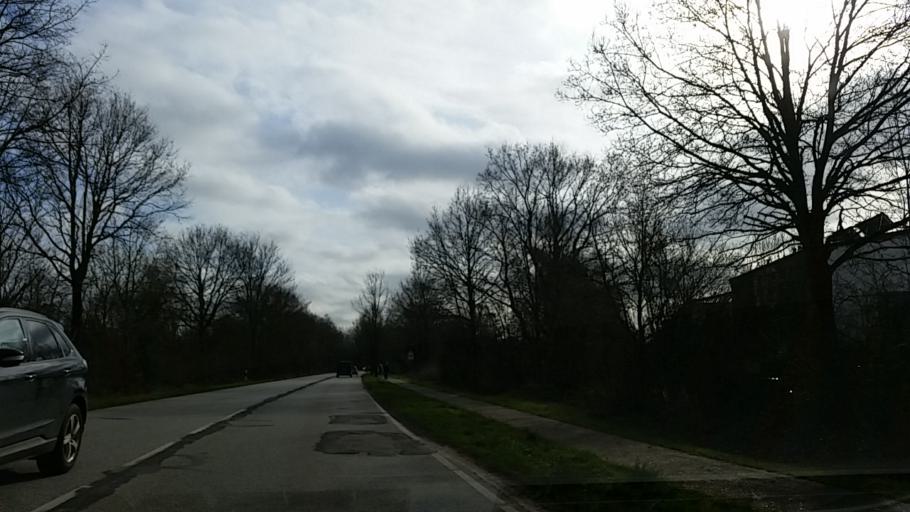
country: DE
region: Schleswig-Holstein
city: Bornsen
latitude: 53.4970
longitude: 10.2697
